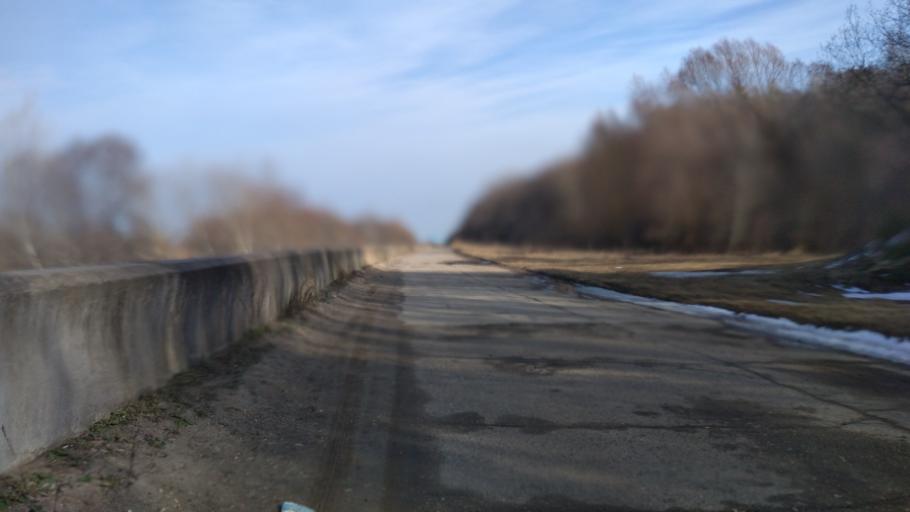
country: RU
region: Chuvashia
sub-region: Cheboksarskiy Rayon
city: Cheboksary
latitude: 56.1462
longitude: 47.3091
